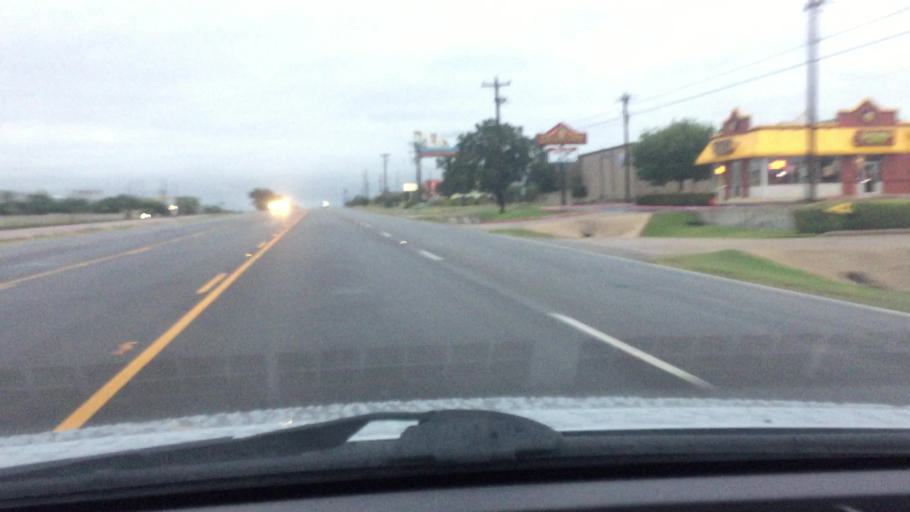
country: US
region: Texas
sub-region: Williamson County
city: Leander
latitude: 30.5675
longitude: -97.8482
